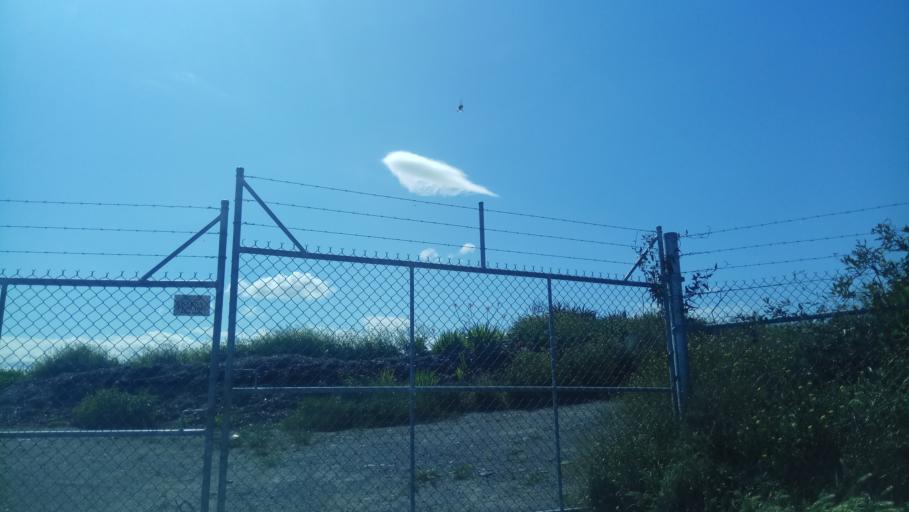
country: AU
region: Victoria
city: Heatherton
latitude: -37.9630
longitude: 145.1171
